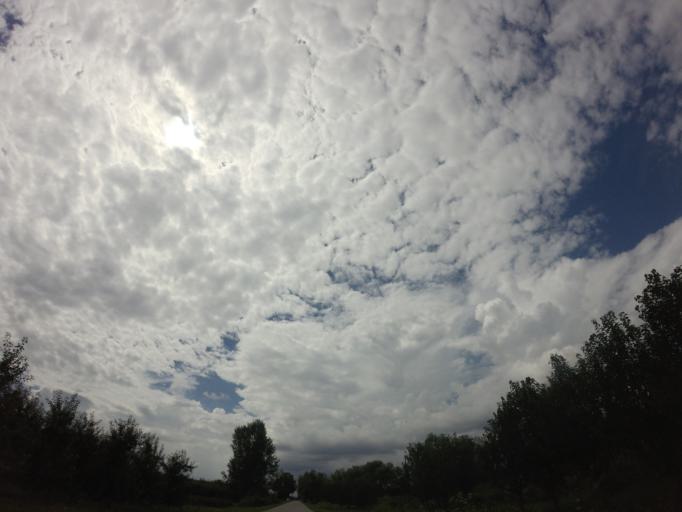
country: PL
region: Lublin Voivodeship
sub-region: Powiat opolski
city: Wilkow
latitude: 51.2410
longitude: 21.8520
